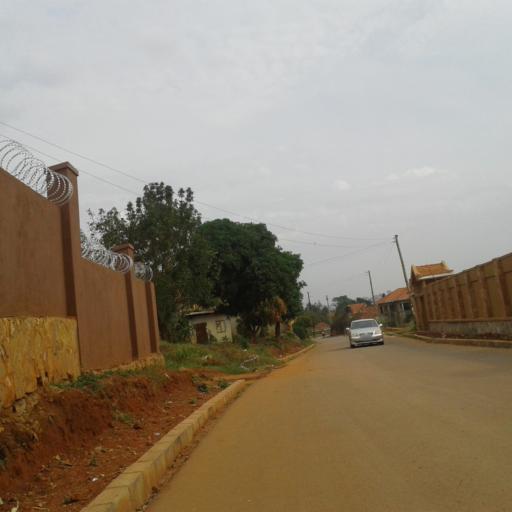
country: UG
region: Central Region
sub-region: Kampala District
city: Kampala
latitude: 0.2728
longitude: 32.6268
